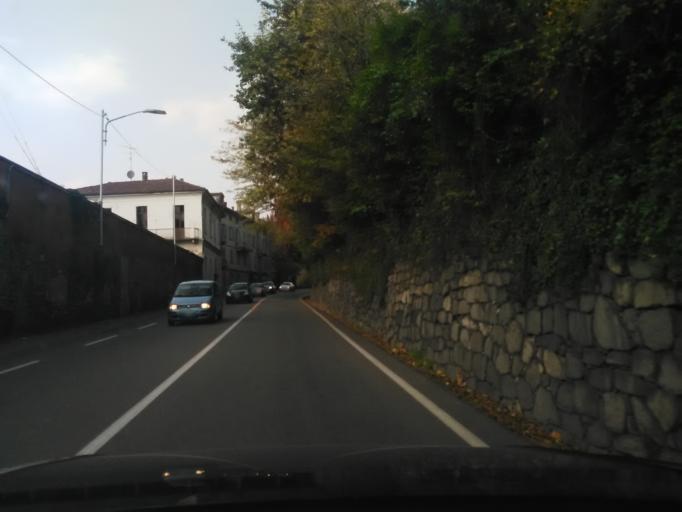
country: IT
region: Piedmont
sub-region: Provincia di Biella
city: Biella
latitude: 45.5764
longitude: 8.0529
